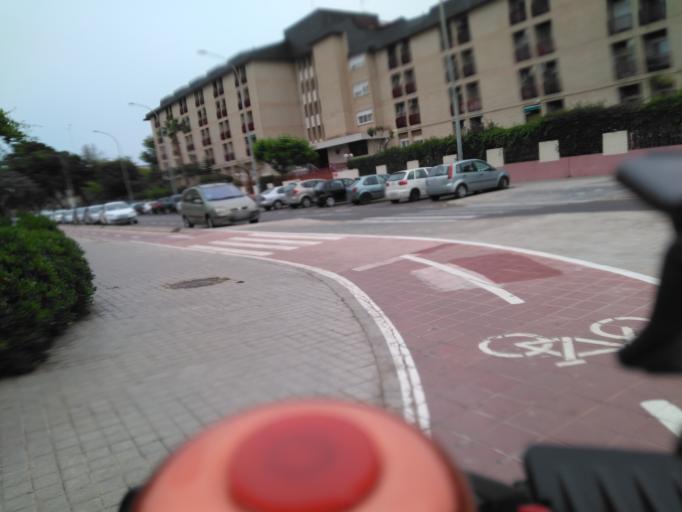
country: ES
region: Valencia
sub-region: Provincia de Valencia
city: Mislata
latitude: 39.4666
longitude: -0.4018
